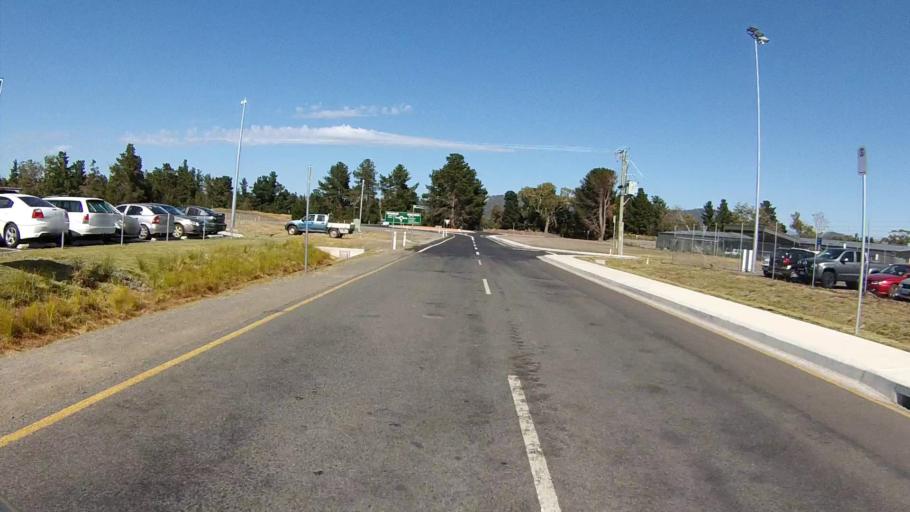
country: AU
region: Tasmania
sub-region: Clarence
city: Seven Mile Beach
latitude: -42.8406
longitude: 147.5039
